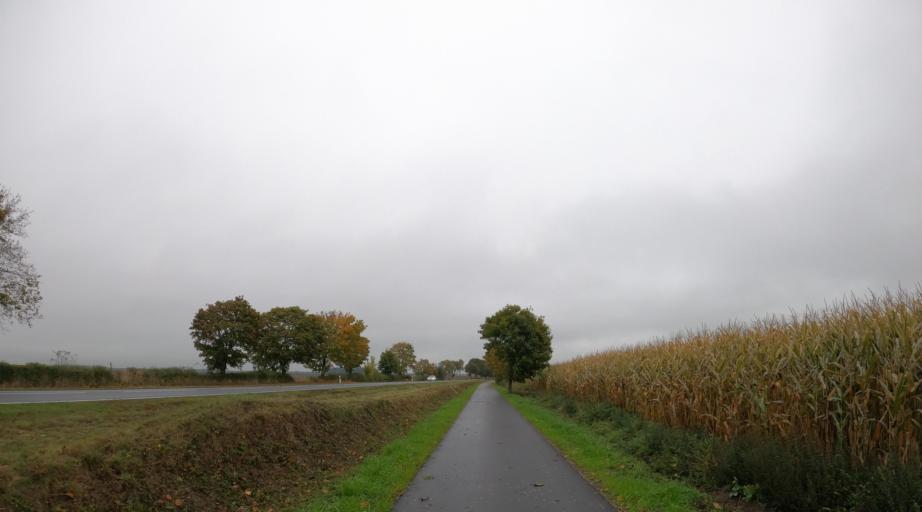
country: PL
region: West Pomeranian Voivodeship
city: Trzcinsko Zdroj
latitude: 52.9705
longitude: 14.6362
